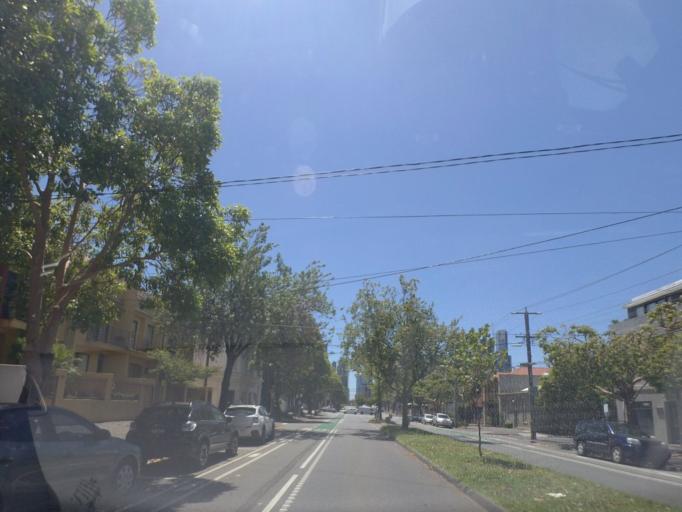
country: AU
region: Victoria
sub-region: Port Phillip
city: South Melbourne
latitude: -37.8354
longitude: 144.9645
